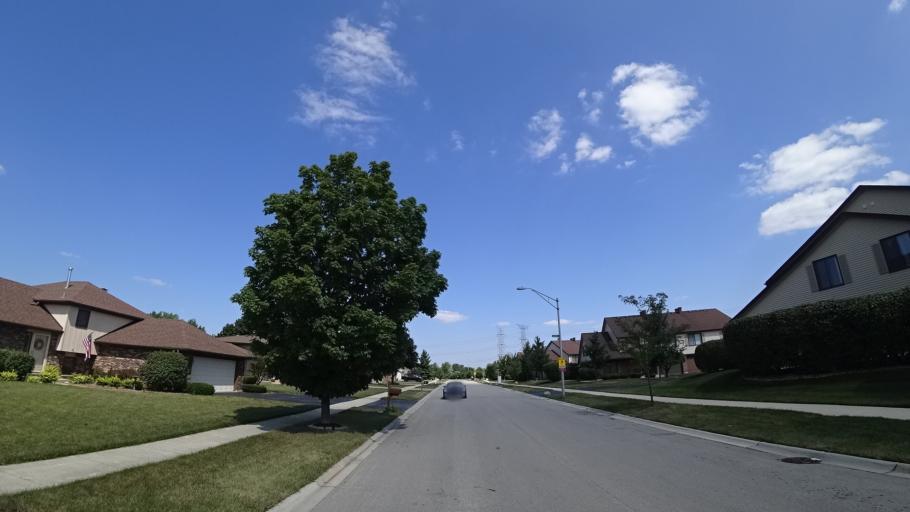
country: US
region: Illinois
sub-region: Cook County
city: Orland Park
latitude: 41.6368
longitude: -87.8469
